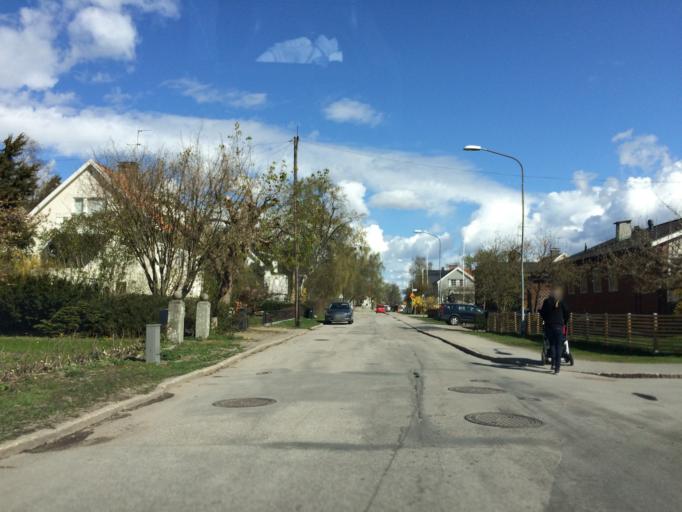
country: SE
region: Stockholm
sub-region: Huddinge Kommun
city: Segeltorp
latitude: 59.2966
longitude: 17.9481
